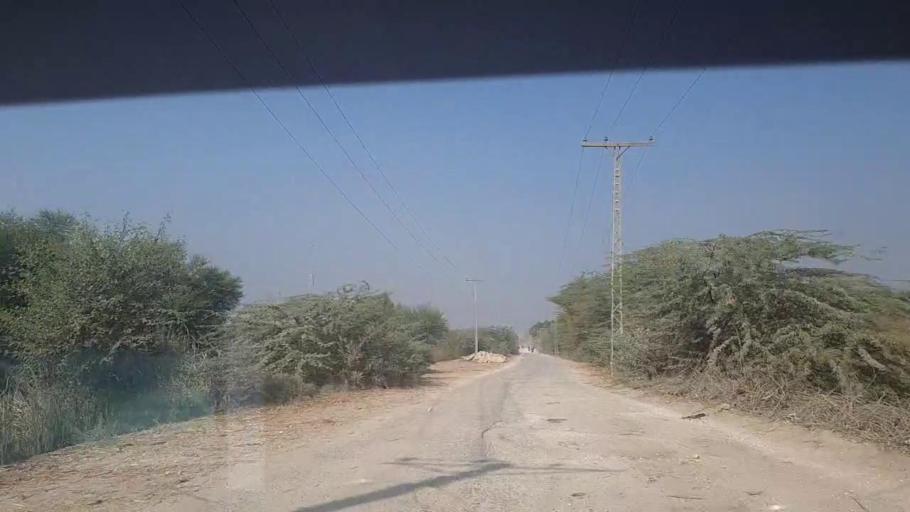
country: PK
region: Sindh
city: Kot Diji
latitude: 27.3557
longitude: 68.7108
